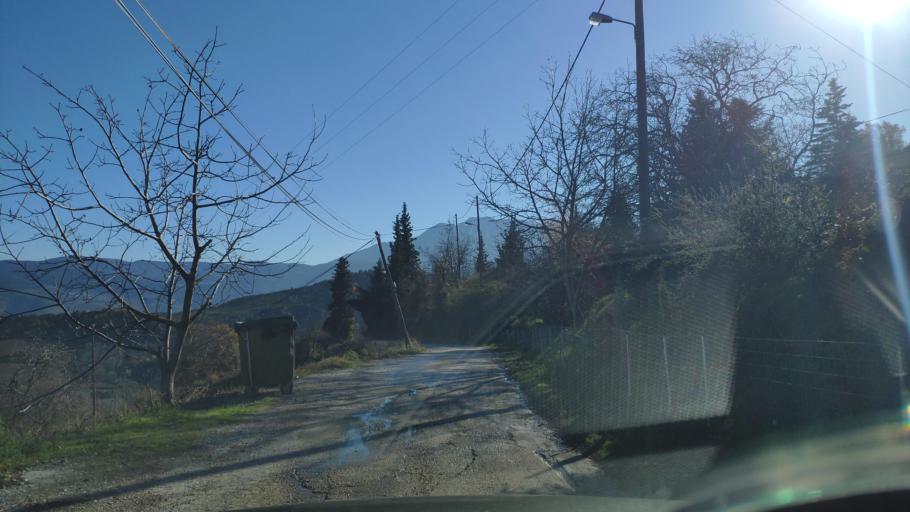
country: GR
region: Peloponnese
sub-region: Nomos Korinthias
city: Xylokastro
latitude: 38.0357
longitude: 22.4747
